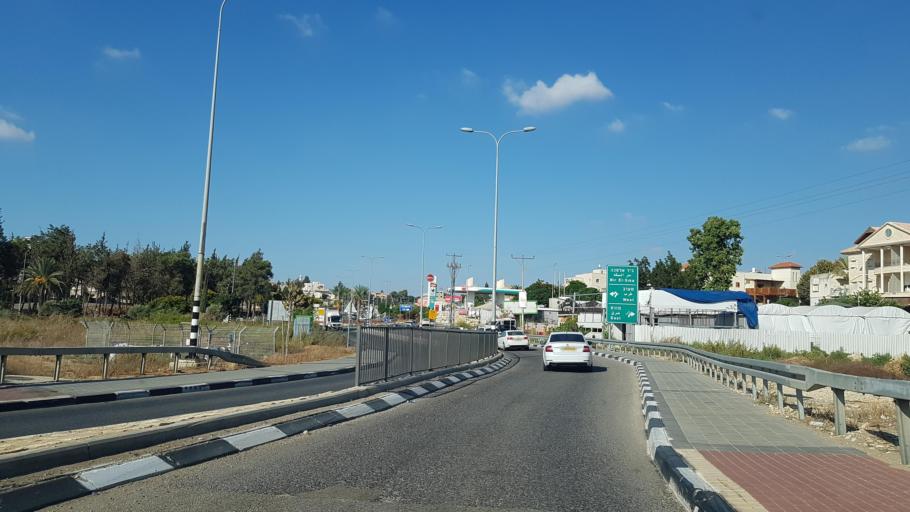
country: PS
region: West Bank
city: Zayta
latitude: 32.3603
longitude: 35.0294
